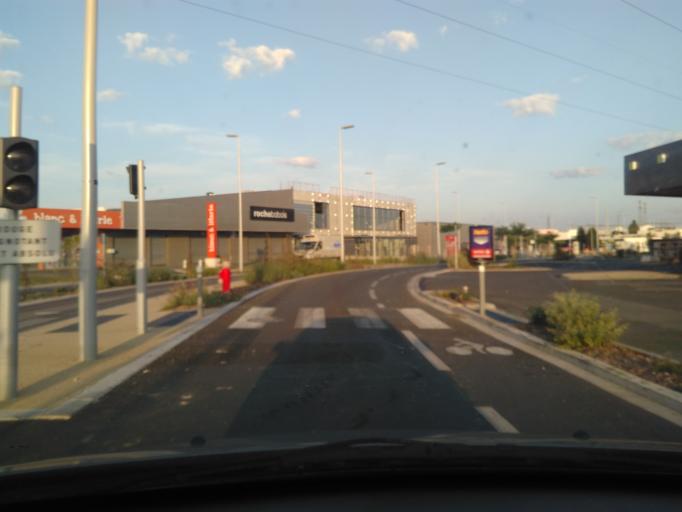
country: FR
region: Poitou-Charentes
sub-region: Departement de la Charente-Maritime
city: Puilboreau
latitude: 46.1761
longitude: -1.1116
